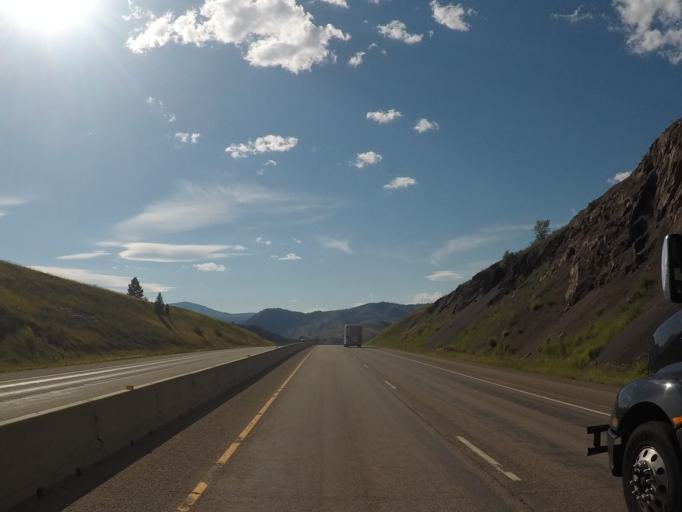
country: US
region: Montana
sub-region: Granite County
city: Philipsburg
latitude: 46.7030
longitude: -113.2460
